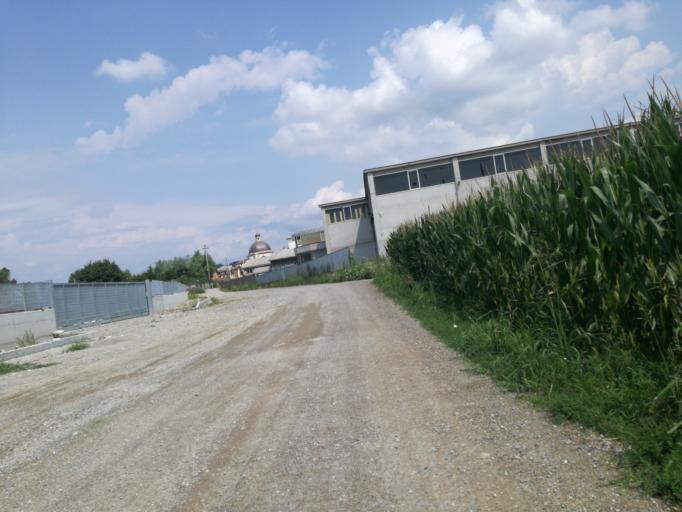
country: IT
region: Lombardy
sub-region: Provincia di Bergamo
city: Calusco d'Adda
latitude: 45.6821
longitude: 9.4739
